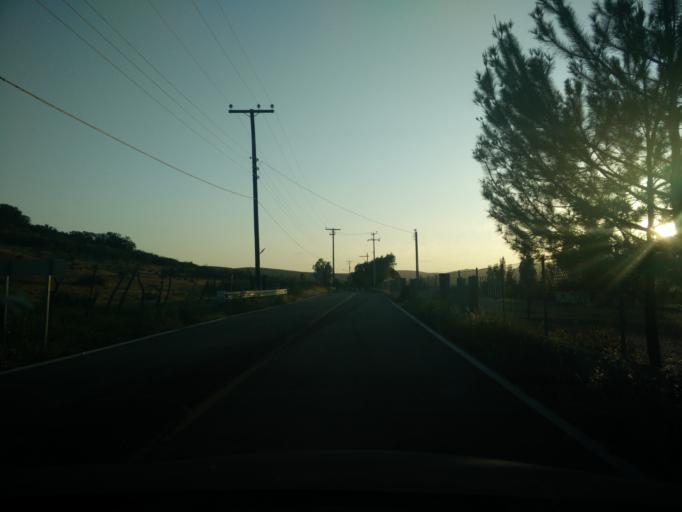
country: MX
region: Baja California
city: El Sauzal
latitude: 32.0104
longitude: -116.6763
